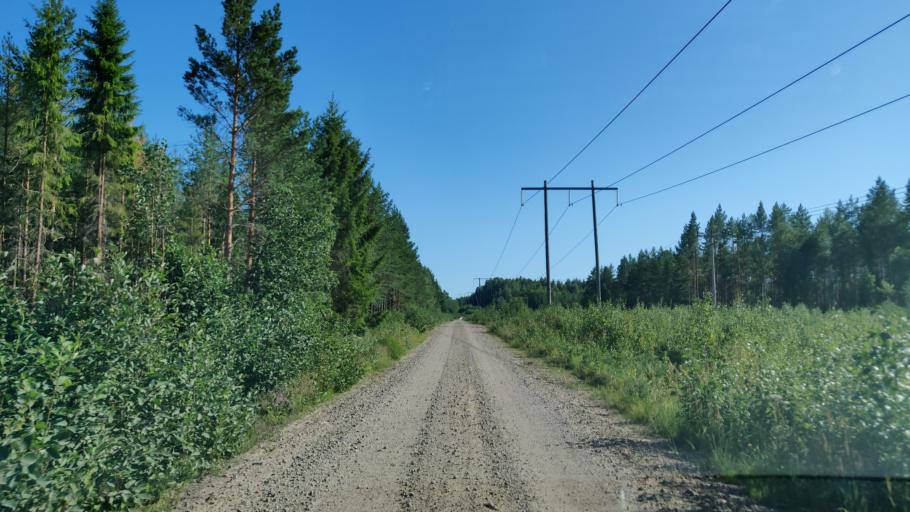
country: SE
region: Vaermland
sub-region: Hagfors Kommun
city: Ekshaerad
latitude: 60.0517
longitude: 13.5225
